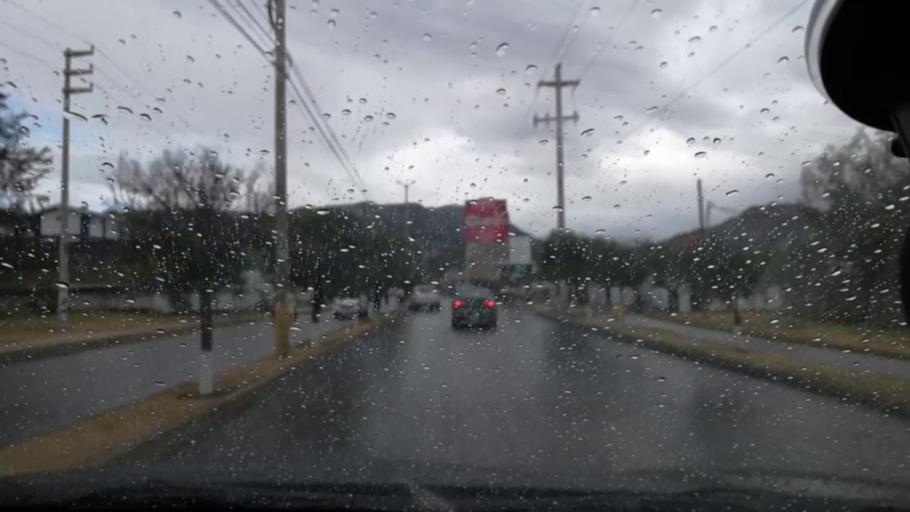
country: PE
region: Cajamarca
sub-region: Provincia de Cajamarca
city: Cajamarca
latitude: -7.1649
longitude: -78.4708
